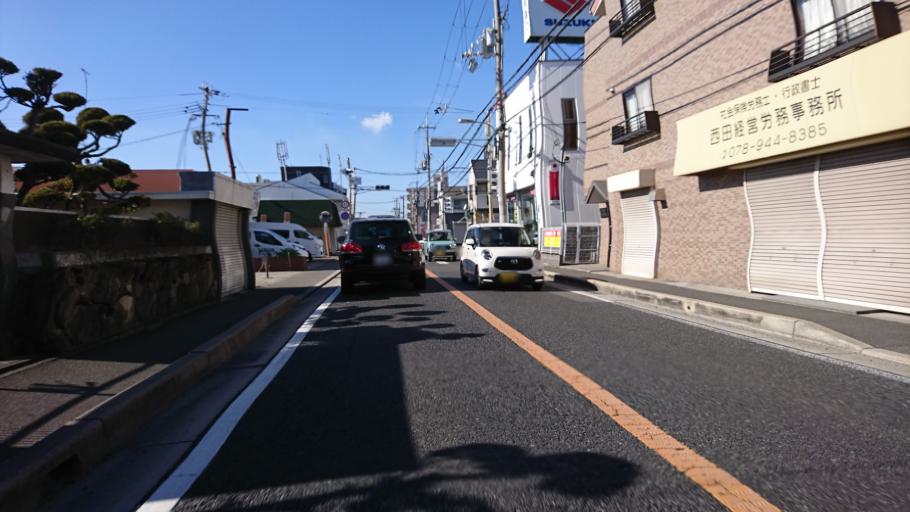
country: JP
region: Hyogo
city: Kakogawacho-honmachi
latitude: 34.7003
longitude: 134.8859
